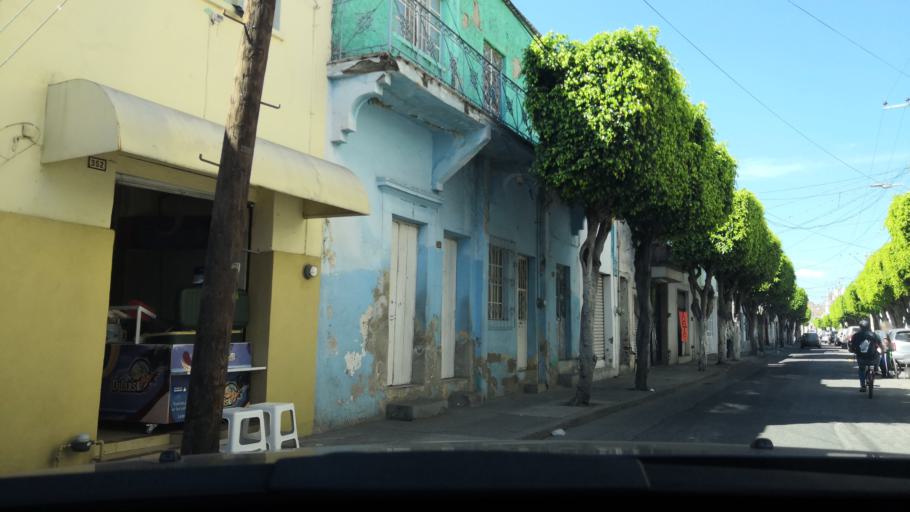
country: MX
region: Guanajuato
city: Leon
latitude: 21.1158
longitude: -101.6800
